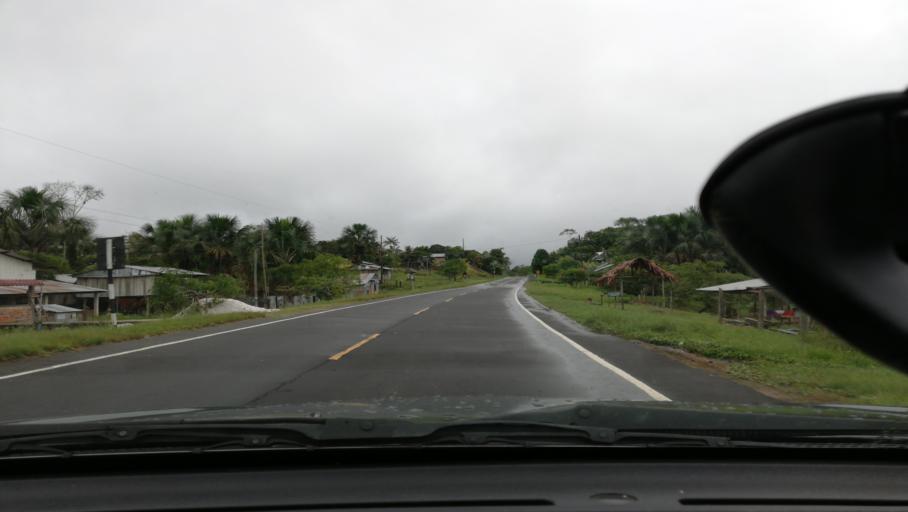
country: PE
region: Loreto
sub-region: Provincia de Loreto
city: Nauta
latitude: -4.2184
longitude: -73.4833
